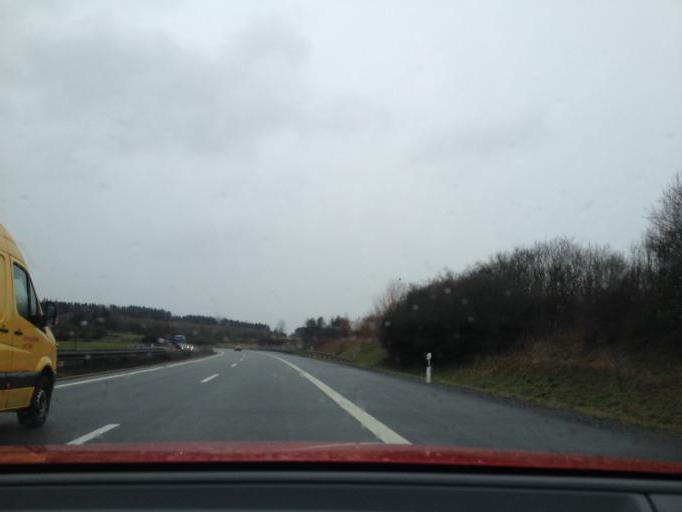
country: DE
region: Bavaria
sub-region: Upper Franconia
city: Schonwald
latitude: 50.2003
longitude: 12.1039
